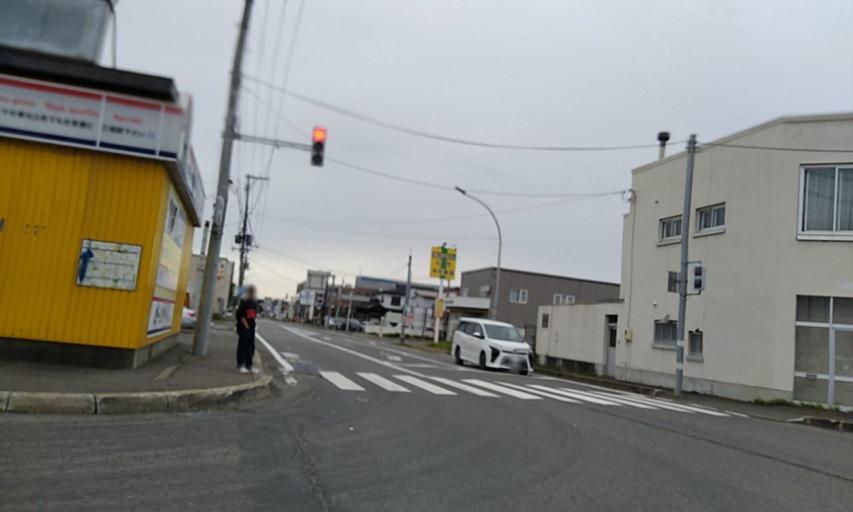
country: JP
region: Hokkaido
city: Bihoro
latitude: 43.8337
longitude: 144.1046
